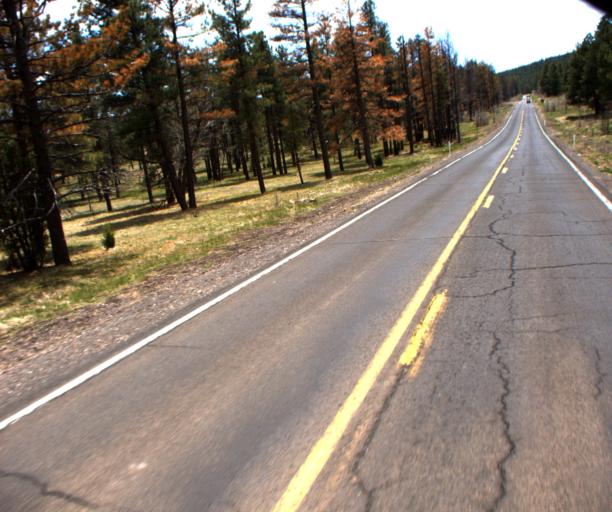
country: US
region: Arizona
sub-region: Coconino County
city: Kachina Village
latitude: 35.0750
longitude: -111.7305
